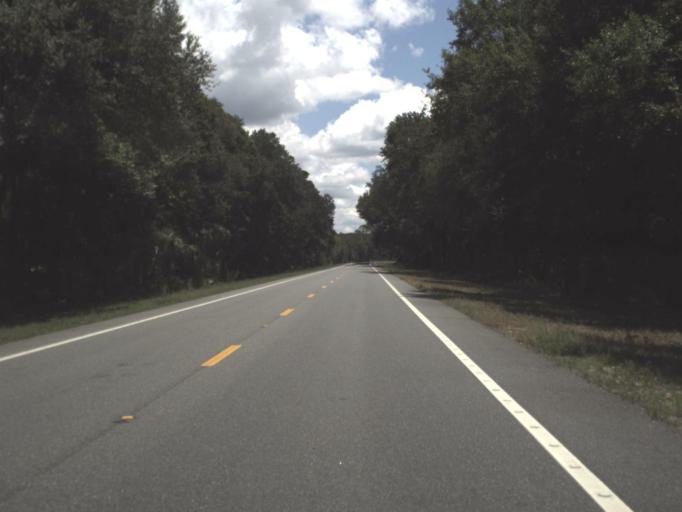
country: US
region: Florida
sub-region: Leon County
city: Woodville
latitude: 30.1441
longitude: -83.9514
